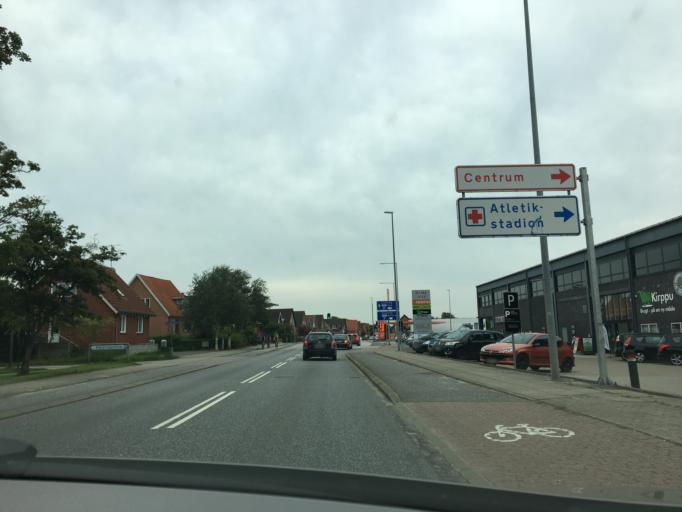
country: DK
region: Central Jutland
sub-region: Herning Kommune
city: Herning
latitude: 56.1461
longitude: 8.9958
